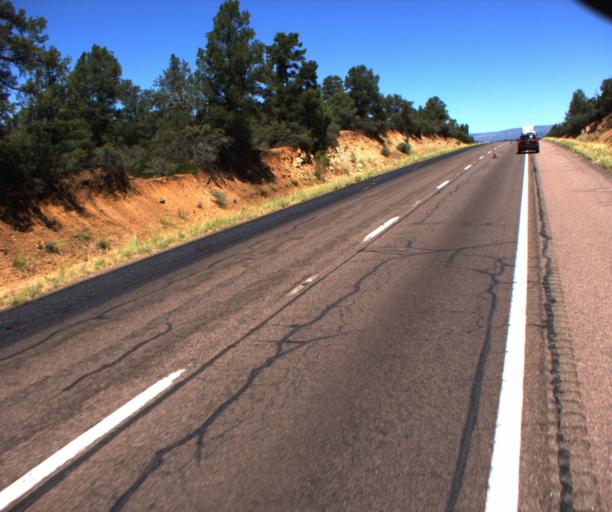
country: US
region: Arizona
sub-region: Gila County
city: Payson
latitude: 34.2041
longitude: -111.3311
